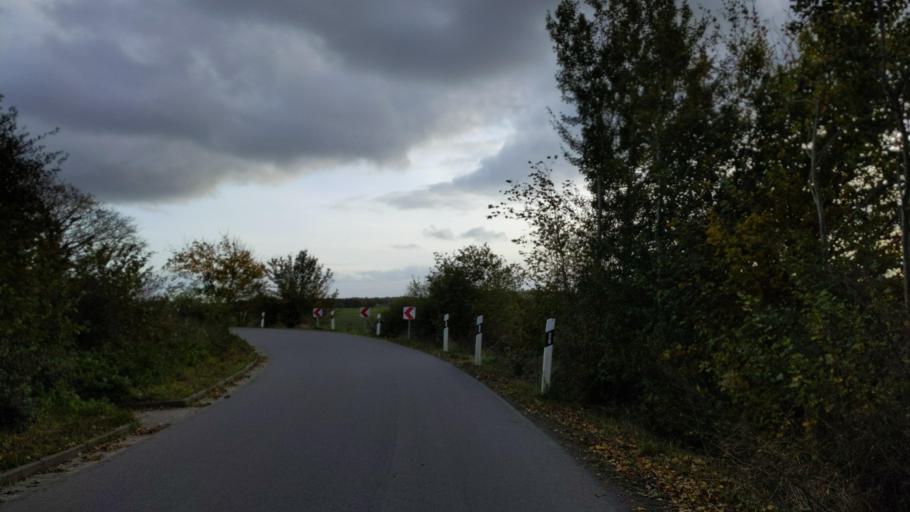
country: DE
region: Schleswig-Holstein
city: Kasseedorf
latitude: 54.1272
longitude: 10.7053
